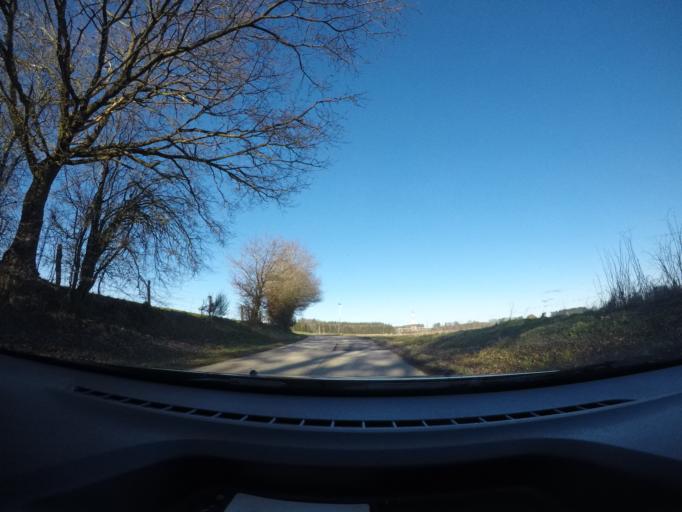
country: BE
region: Wallonia
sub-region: Province du Luxembourg
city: Bertrix
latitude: 49.8407
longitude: 5.2990
